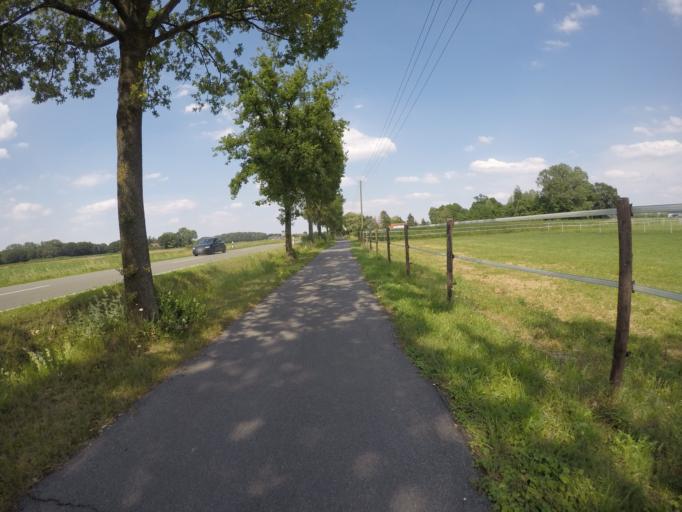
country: DE
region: North Rhine-Westphalia
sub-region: Regierungsbezirk Munster
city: Heiden
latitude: 51.8734
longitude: 6.9095
